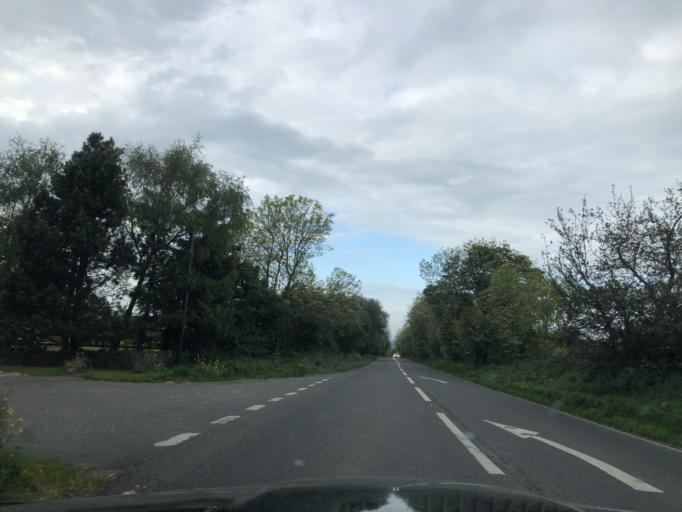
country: GB
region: England
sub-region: Gloucestershire
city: Stow on the Wold
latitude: 51.9393
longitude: -1.7219
